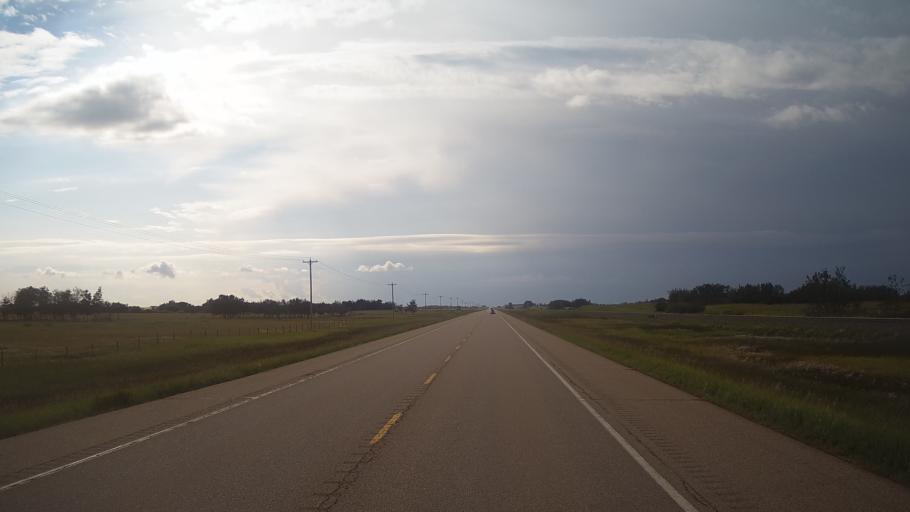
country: CA
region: Alberta
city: Viking
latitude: 53.1470
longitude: -111.9588
